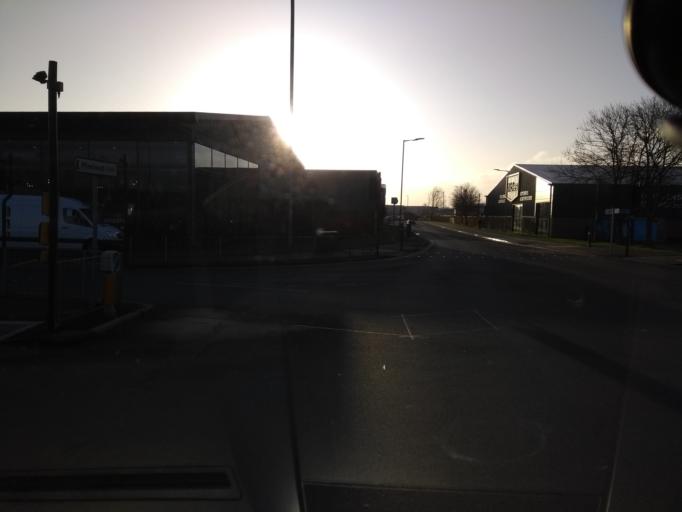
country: GB
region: England
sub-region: Somerset
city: Bridgwater
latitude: 51.1371
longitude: -2.9995
